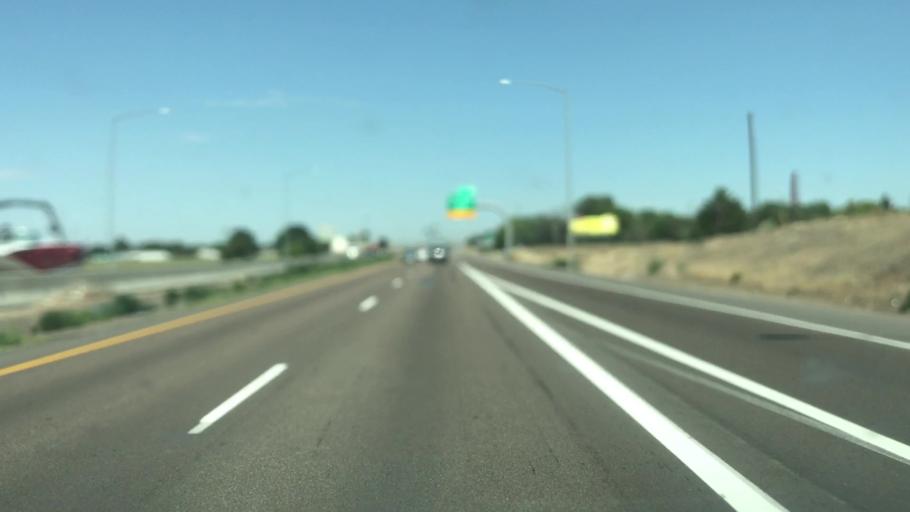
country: US
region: Idaho
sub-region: Canyon County
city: Caldwell
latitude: 43.6645
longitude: -116.6635
